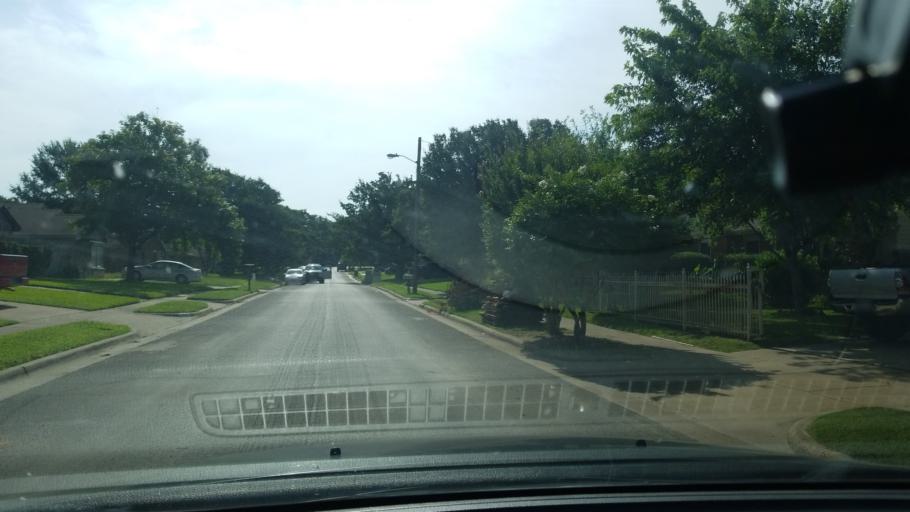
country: US
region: Texas
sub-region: Dallas County
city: Balch Springs
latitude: 32.7305
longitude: -96.6411
